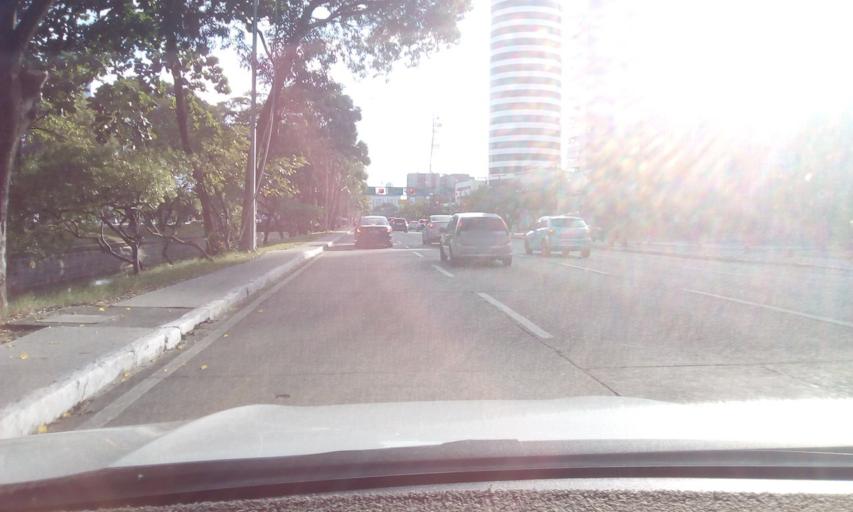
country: BR
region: Pernambuco
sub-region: Recife
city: Recife
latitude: -8.0477
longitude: -34.8924
